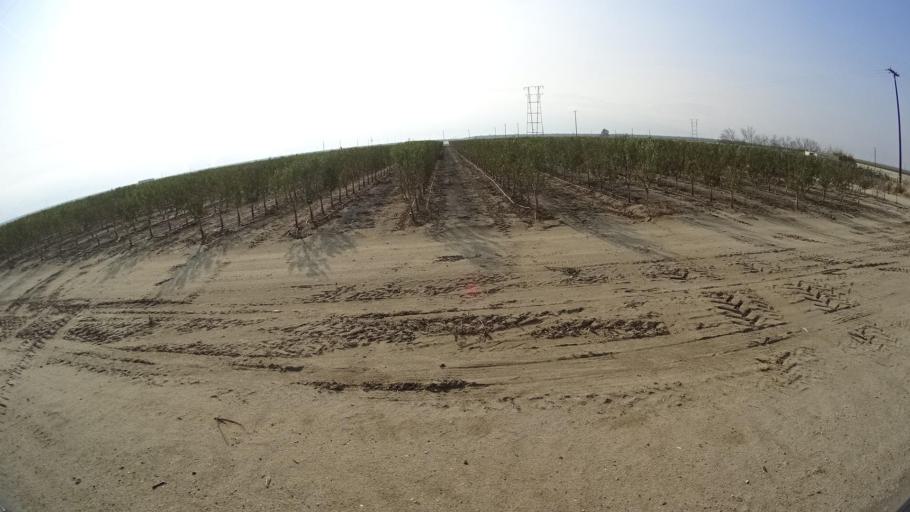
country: US
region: California
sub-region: Kern County
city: Lebec
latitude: 34.9930
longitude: -118.8729
